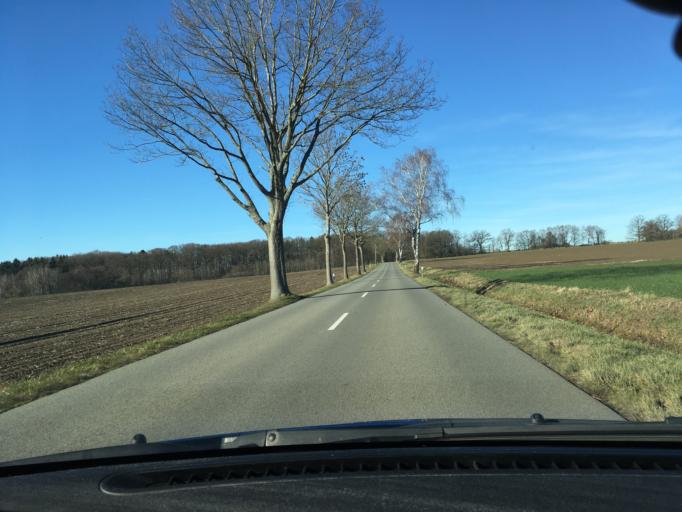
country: DE
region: Lower Saxony
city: Schwienau
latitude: 52.9705
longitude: 10.4551
